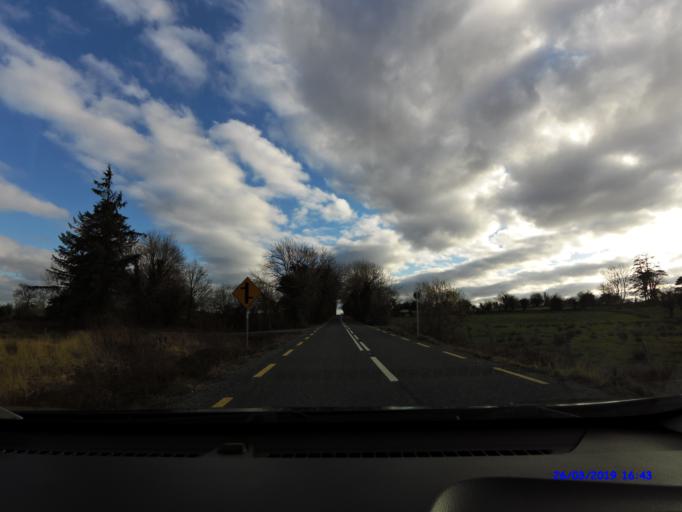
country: IE
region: Connaught
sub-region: Maigh Eo
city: Ballyhaunis
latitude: 53.8556
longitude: -8.7665
